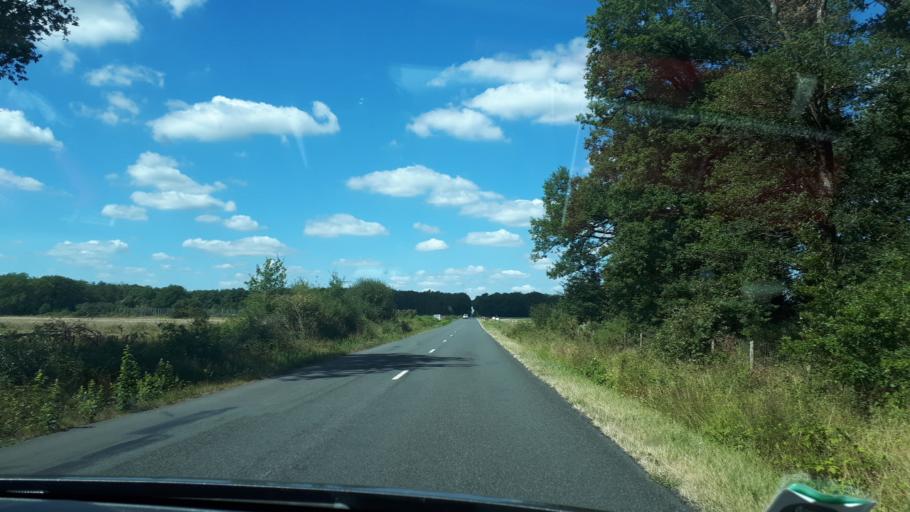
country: FR
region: Centre
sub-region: Departement du Loir-et-Cher
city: Neung-sur-Beuvron
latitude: 47.5341
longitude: 1.7343
